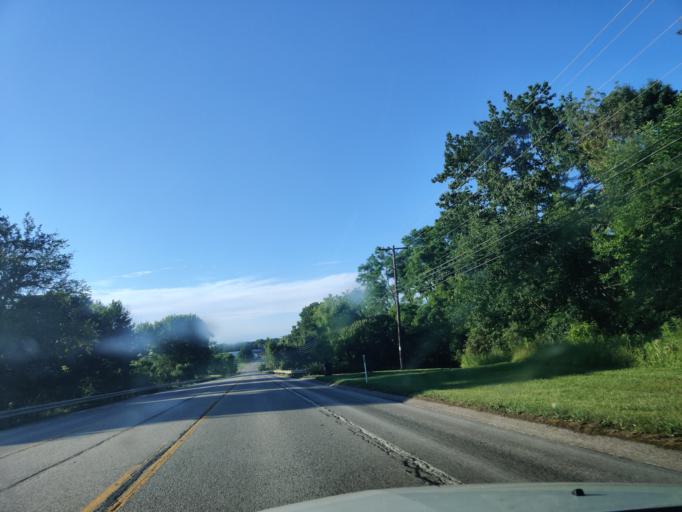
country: US
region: Pennsylvania
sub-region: Lawrence County
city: New Castle Northwest
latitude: 41.0726
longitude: -80.3615
